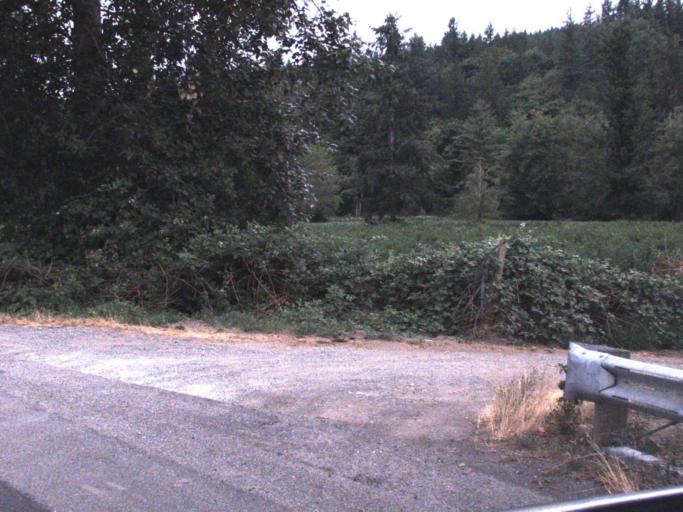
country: US
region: Washington
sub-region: King County
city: Fall City
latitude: 47.5917
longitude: -121.9067
